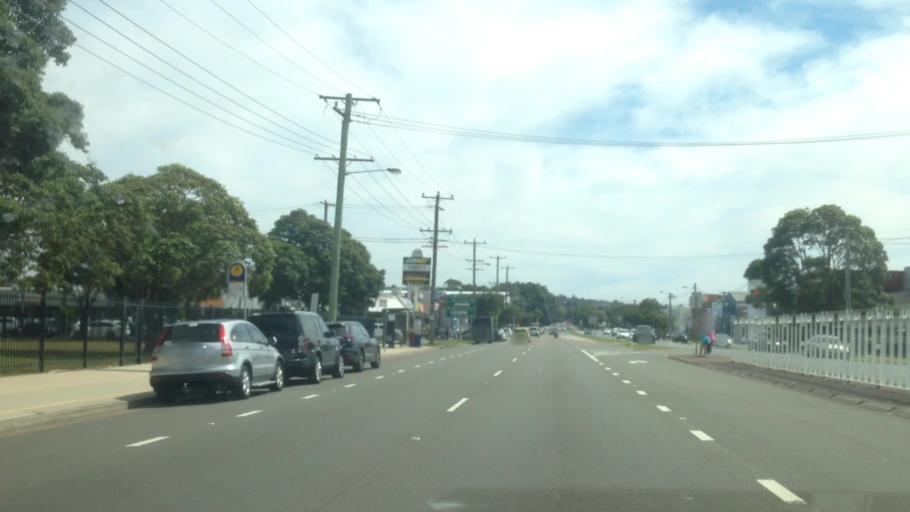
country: AU
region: New South Wales
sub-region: Newcastle
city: Broadmeadow
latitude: -32.9237
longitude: 151.7270
